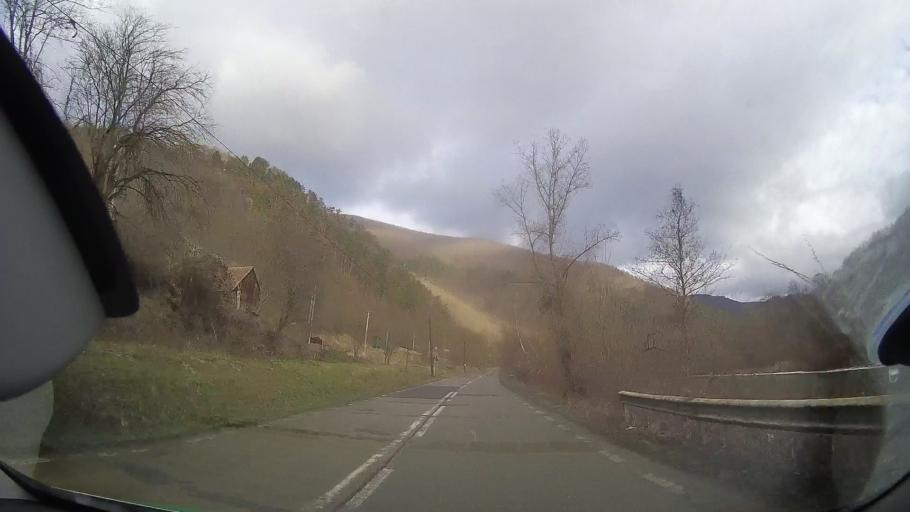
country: RO
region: Cluj
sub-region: Comuna Iara
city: Iara
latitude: 46.5001
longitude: 23.5399
